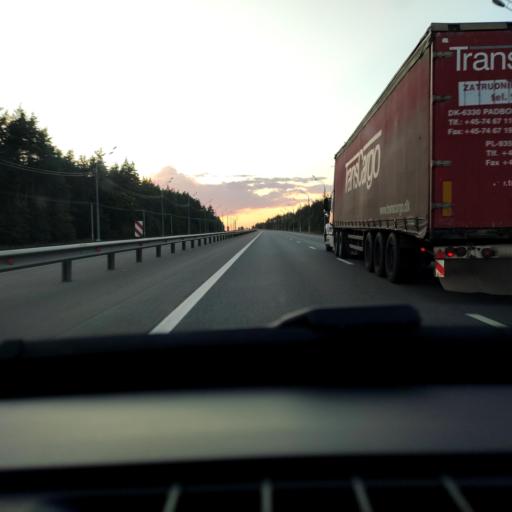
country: RU
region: Lipetsk
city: Zadonsk
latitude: 52.3519
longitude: 38.9467
